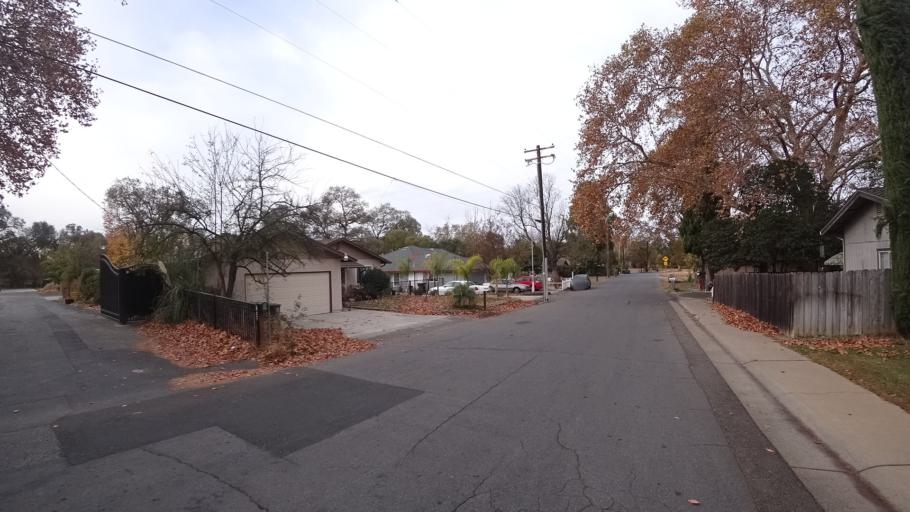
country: US
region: California
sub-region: Sacramento County
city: Citrus Heights
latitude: 38.7098
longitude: -121.2843
